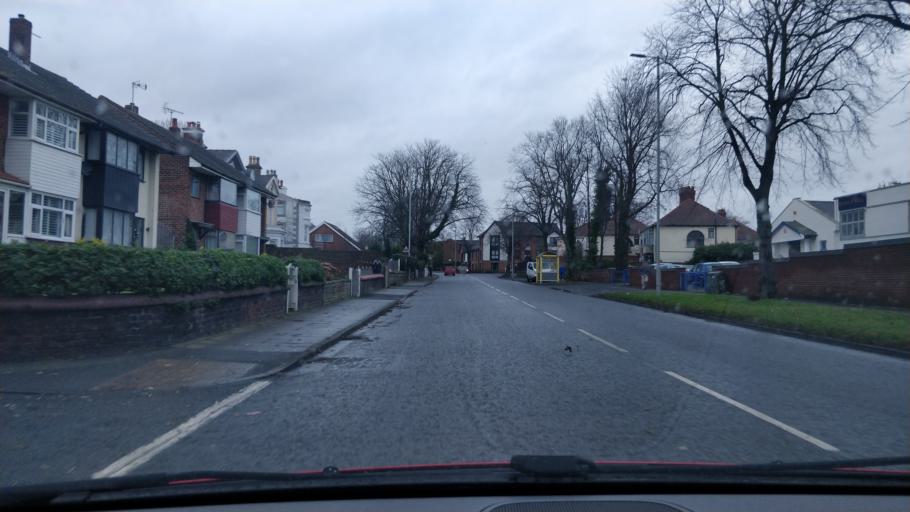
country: GB
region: England
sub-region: Sefton
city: Litherland
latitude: 53.4717
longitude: -2.9993
